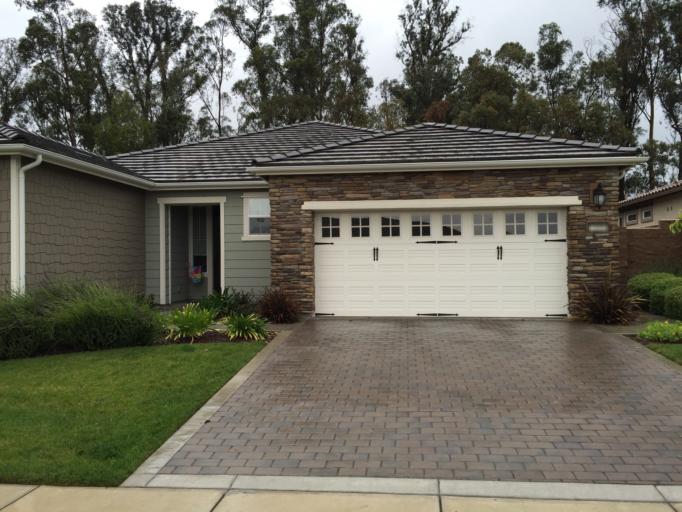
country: US
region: California
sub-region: San Luis Obispo County
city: Callender
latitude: 35.0345
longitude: -120.5460
